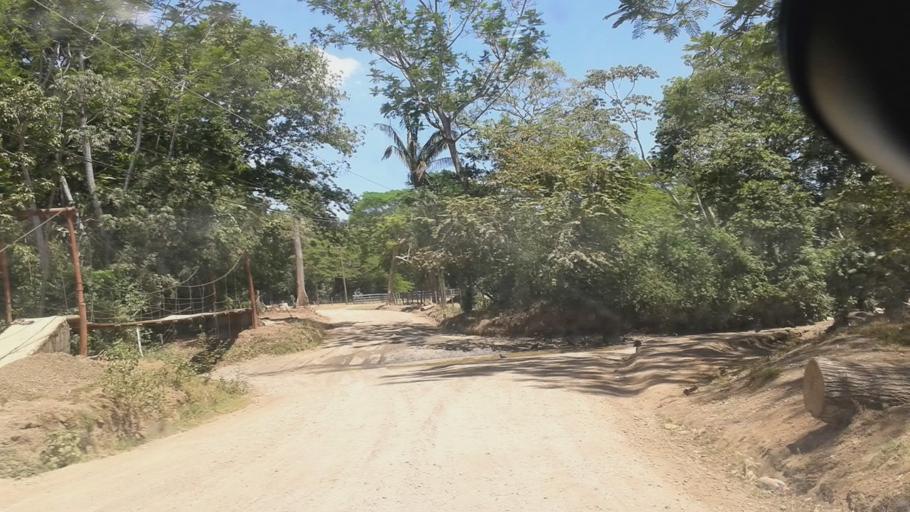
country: CR
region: Guanacaste
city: Samara
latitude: 9.9975
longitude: -85.6947
